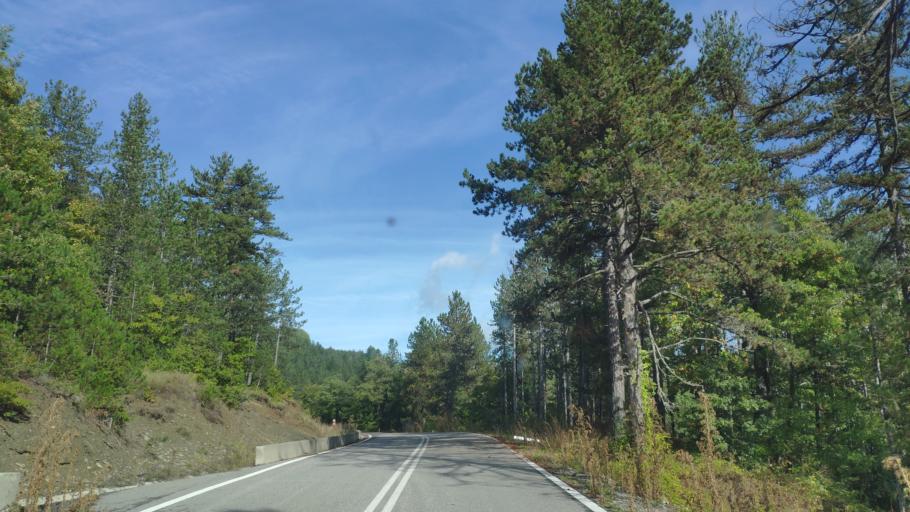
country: AL
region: Korce
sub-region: Rrethi i Devollit
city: Miras
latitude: 40.3690
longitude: 20.9254
